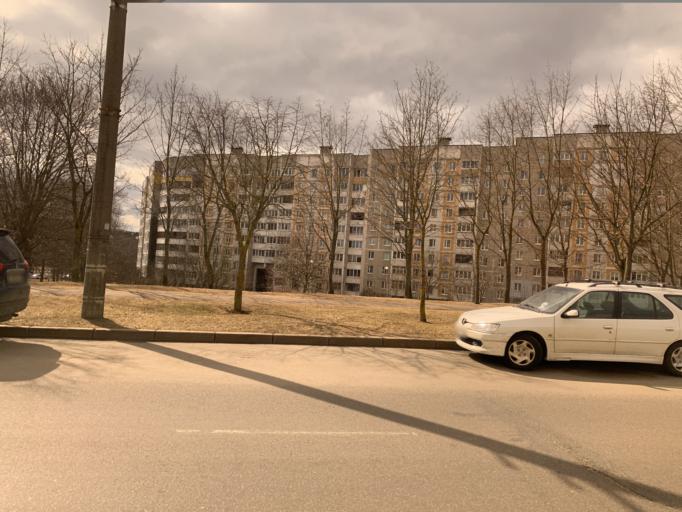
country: BY
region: Minsk
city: Borovlyany
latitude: 53.9344
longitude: 27.6885
